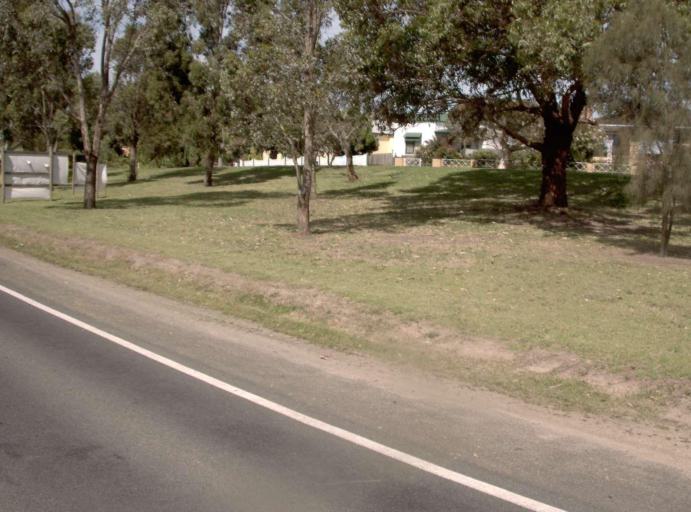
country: AU
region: Victoria
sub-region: East Gippsland
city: Bairnsdale
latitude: -37.8216
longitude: 147.6479
